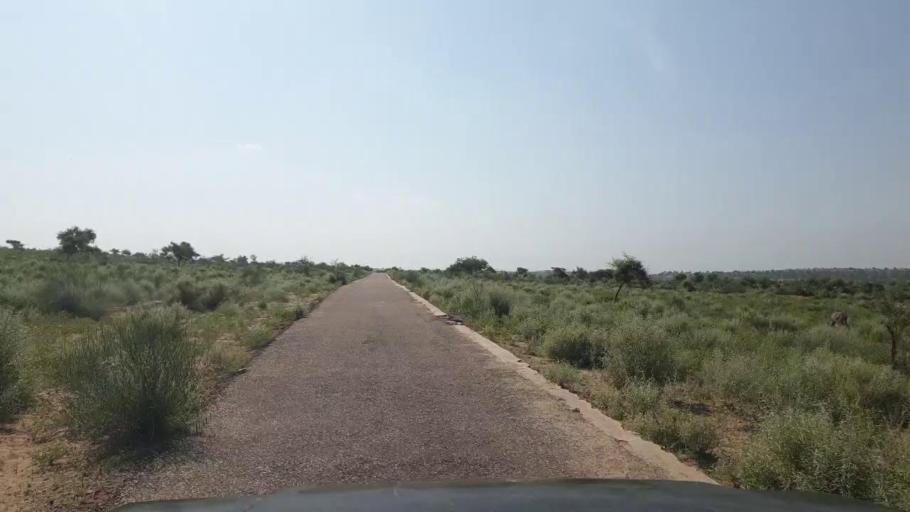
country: PK
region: Sindh
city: Islamkot
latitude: 25.1767
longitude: 70.3960
